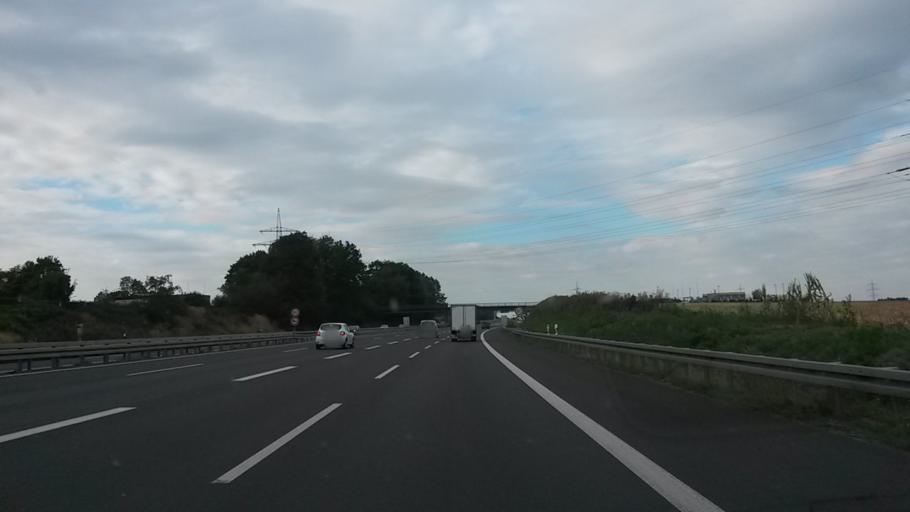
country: DE
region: North Rhine-Westphalia
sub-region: Regierungsbezirk Koln
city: Wurselen
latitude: 50.7960
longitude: 6.1695
